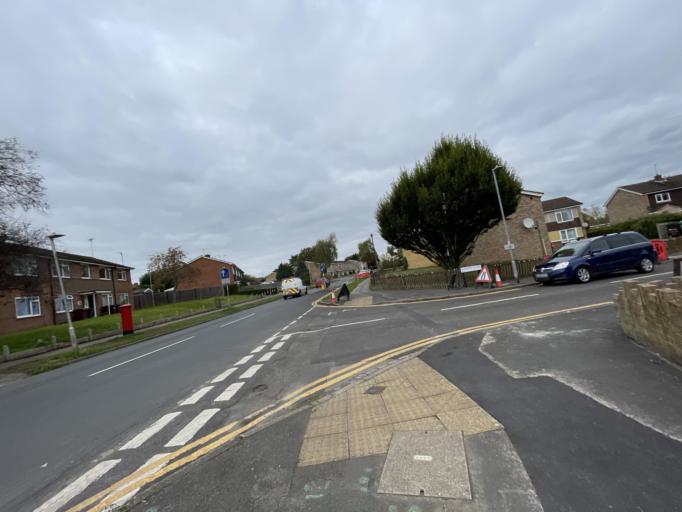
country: GB
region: England
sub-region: West Berkshire
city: Tilehurst
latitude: 51.4554
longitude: -1.0364
